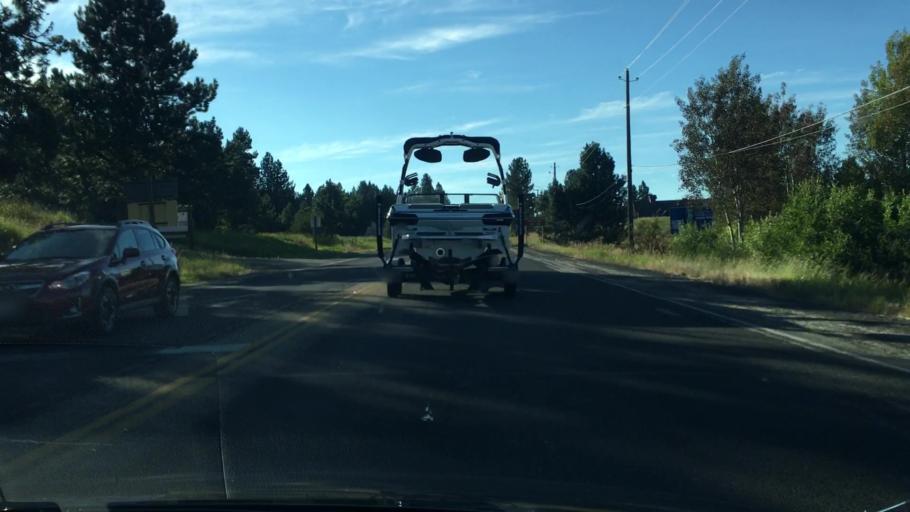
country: US
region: Idaho
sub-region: Valley County
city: Cascade
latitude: 44.5075
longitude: -116.0326
